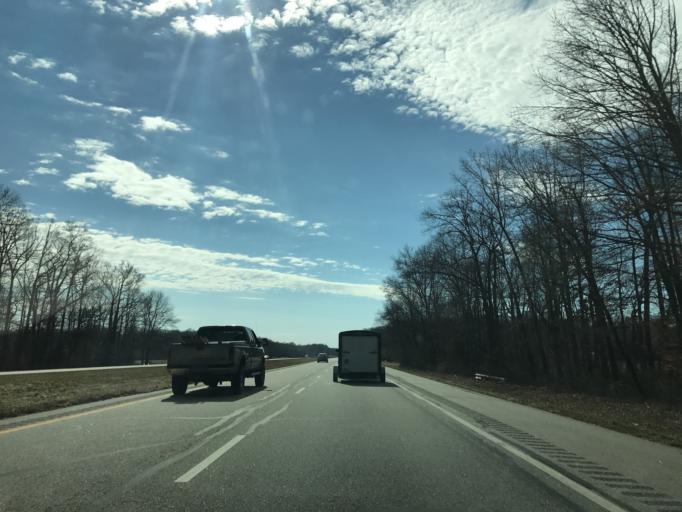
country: US
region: Delaware
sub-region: New Castle County
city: Townsend
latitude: 39.2970
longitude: -75.8528
